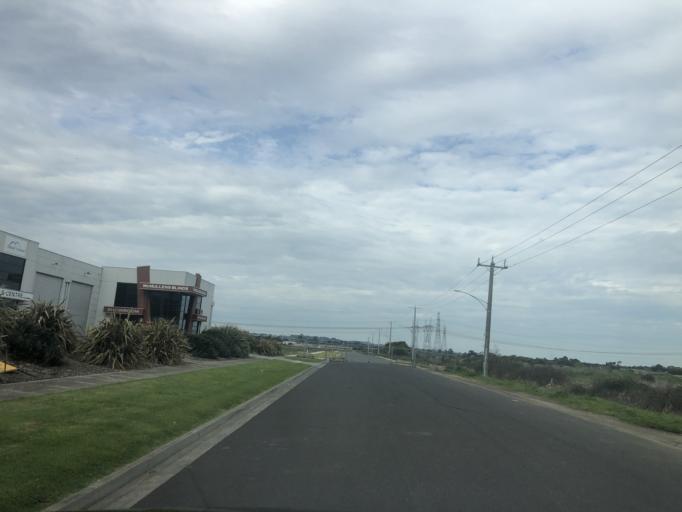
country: AU
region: Victoria
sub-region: Casey
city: Hallam
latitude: -38.0208
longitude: 145.2791
